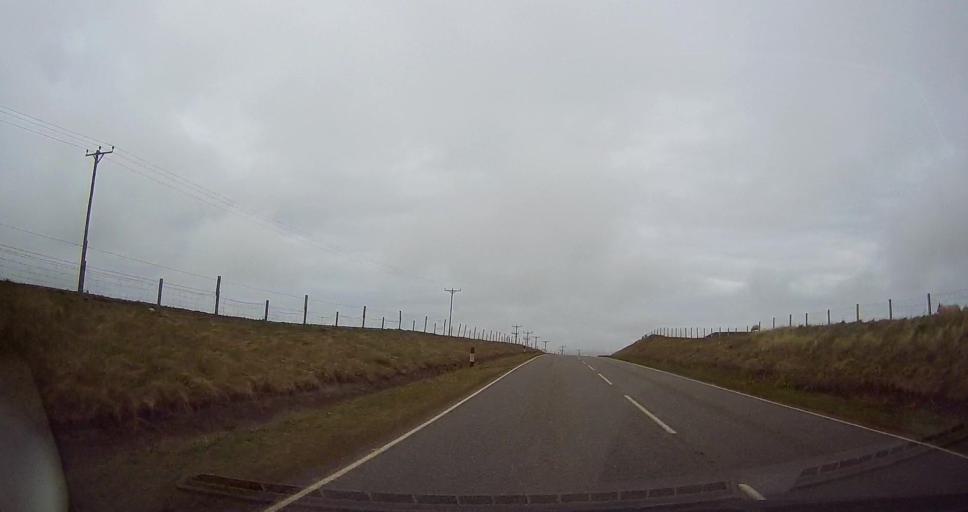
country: GB
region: Scotland
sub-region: Shetland Islands
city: Sandwick
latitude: 59.8960
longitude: -1.3031
